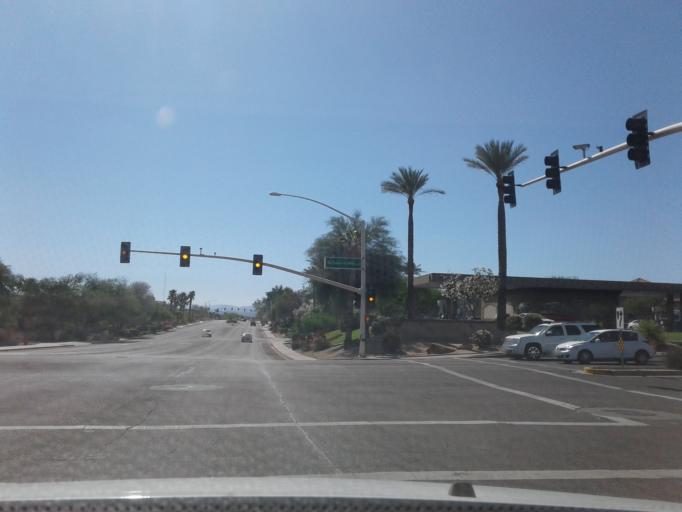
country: US
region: Arizona
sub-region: Maricopa County
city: Fountain Hills
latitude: 33.6113
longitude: -111.7292
